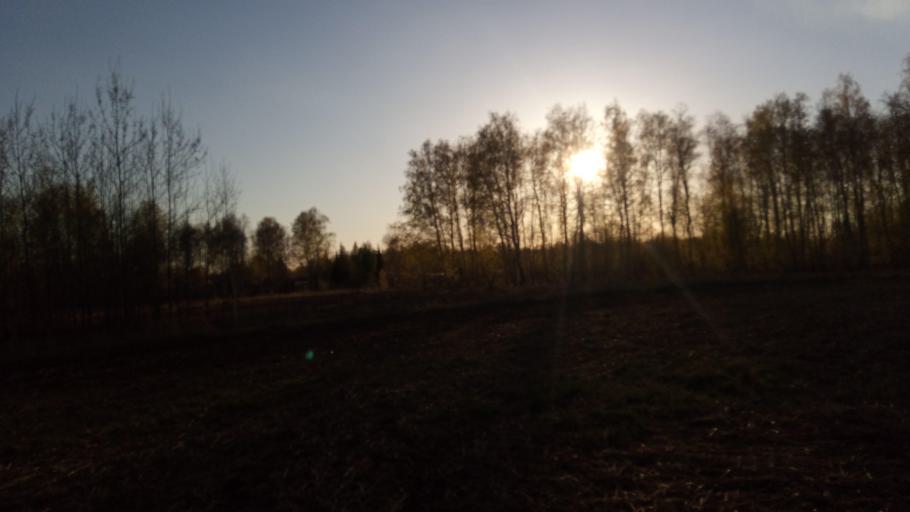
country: RU
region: Chelyabinsk
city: Timiryazevskiy
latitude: 54.9942
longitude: 60.8618
